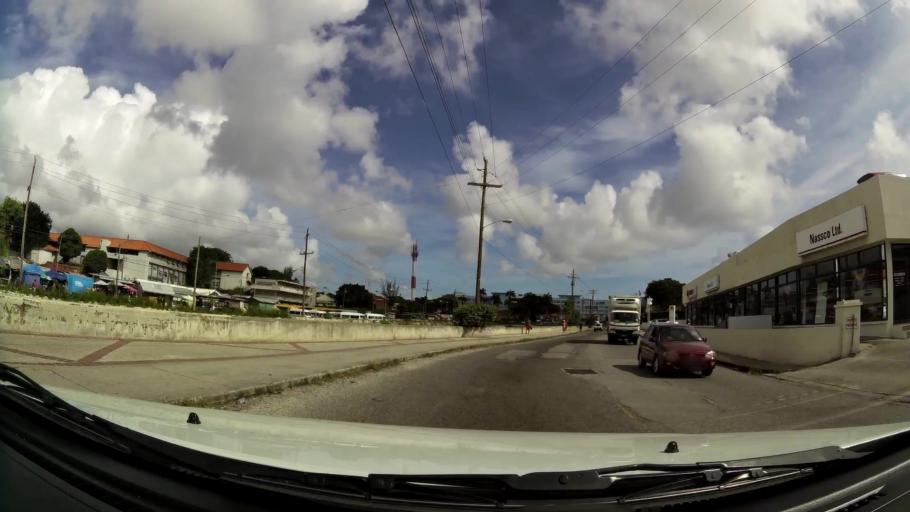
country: BB
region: Saint Michael
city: Bridgetown
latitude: 13.0967
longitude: -59.6101
